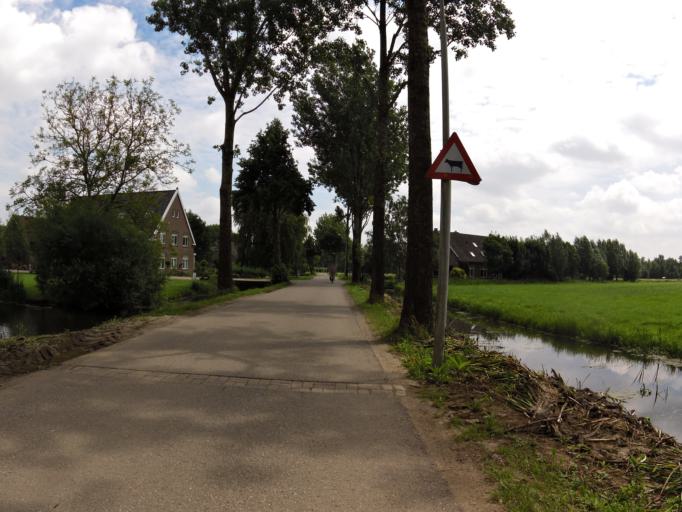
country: NL
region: South Holland
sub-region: Gemeente Leerdam
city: Leerdam
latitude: 51.9051
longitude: 5.0699
